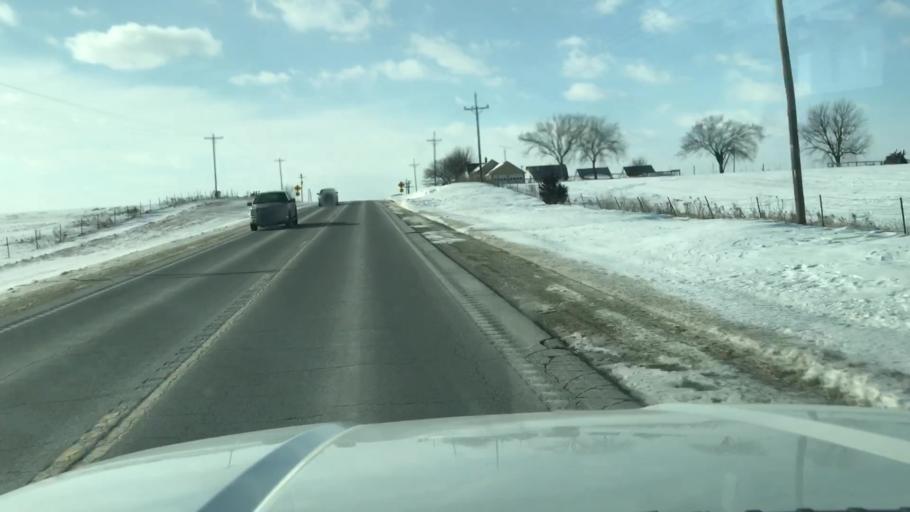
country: US
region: Missouri
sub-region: Nodaway County
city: Maryville
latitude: 40.3442
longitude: -94.7572
